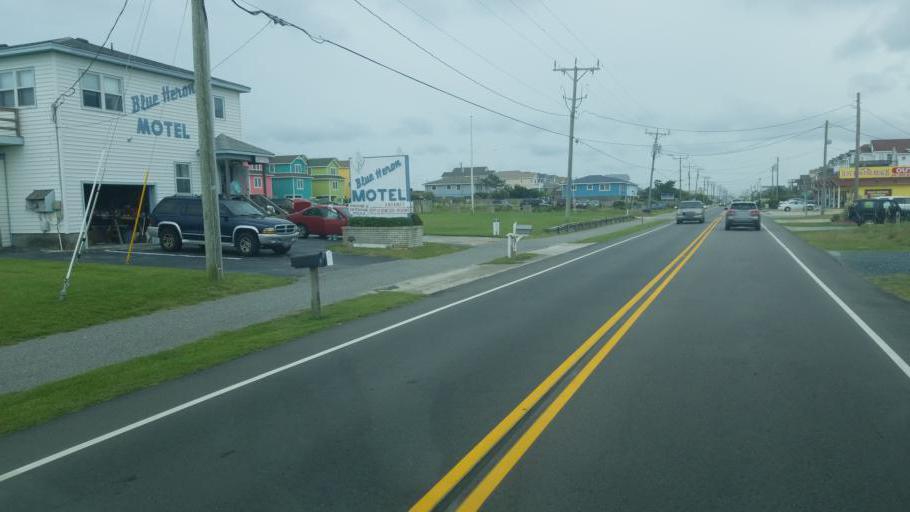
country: US
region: North Carolina
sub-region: Dare County
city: Nags Head
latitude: 35.9181
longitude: -75.6021
